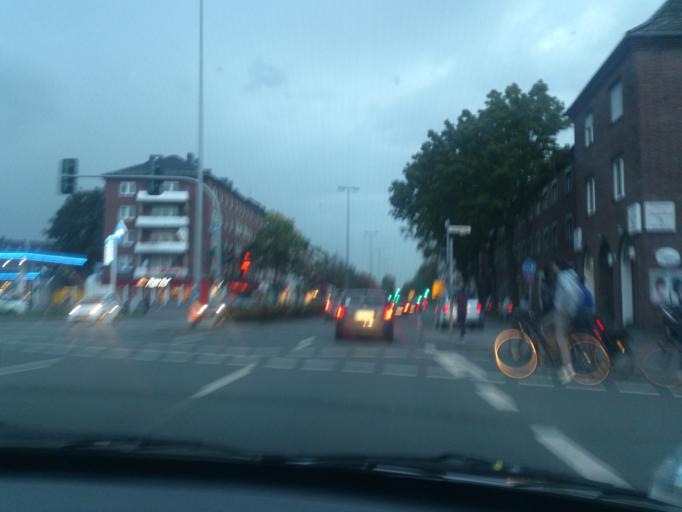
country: DE
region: North Rhine-Westphalia
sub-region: Regierungsbezirk Munster
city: Muenster
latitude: 51.9673
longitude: 7.6154
